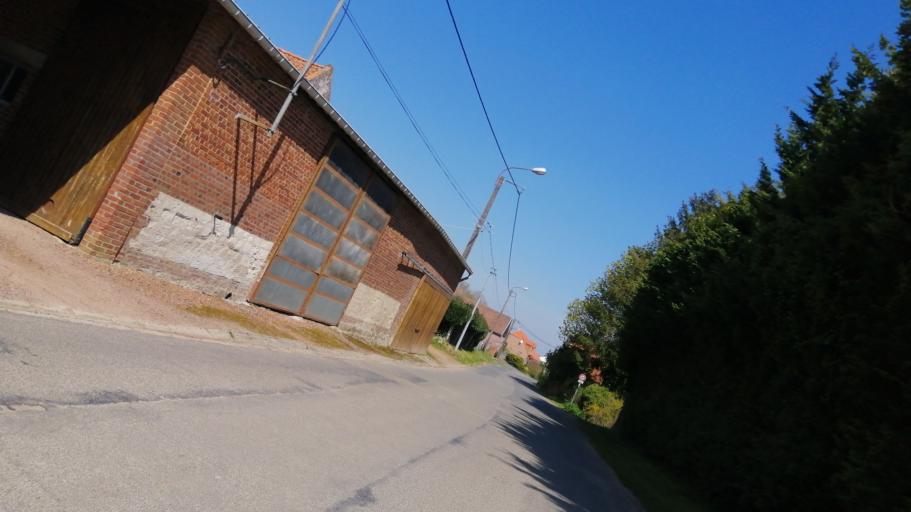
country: FR
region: Nord-Pas-de-Calais
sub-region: Departement du Pas-de-Calais
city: Duisans
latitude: 50.3099
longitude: 2.6516
